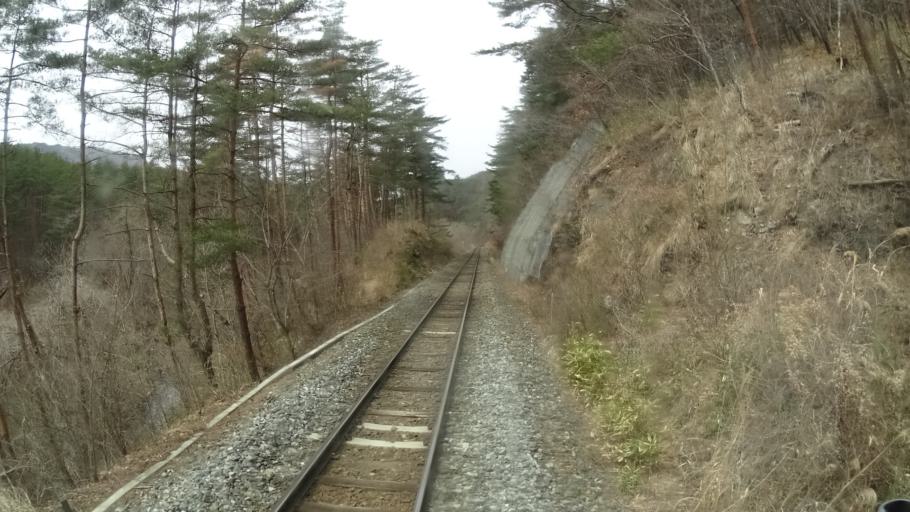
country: JP
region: Iwate
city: Tono
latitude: 39.3359
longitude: 141.3561
